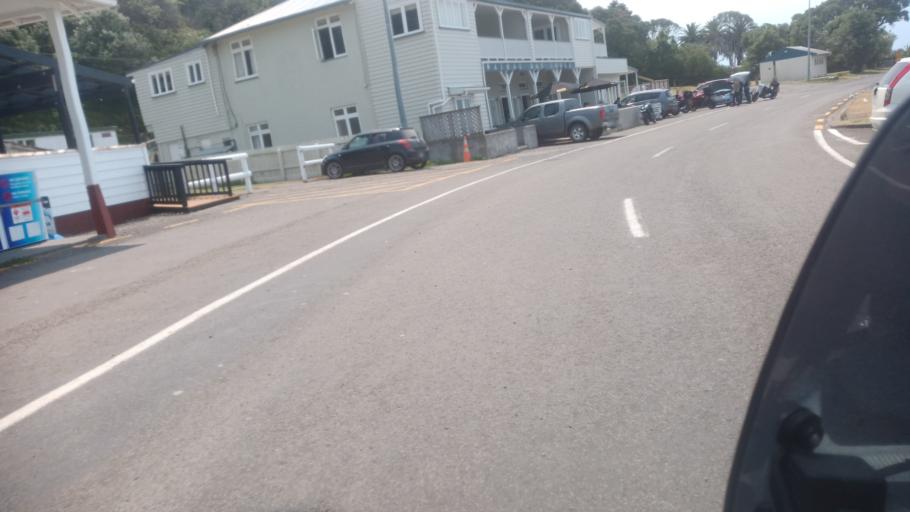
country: NZ
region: Bay of Plenty
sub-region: Opotiki District
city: Opotiki
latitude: -37.6161
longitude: 177.9075
